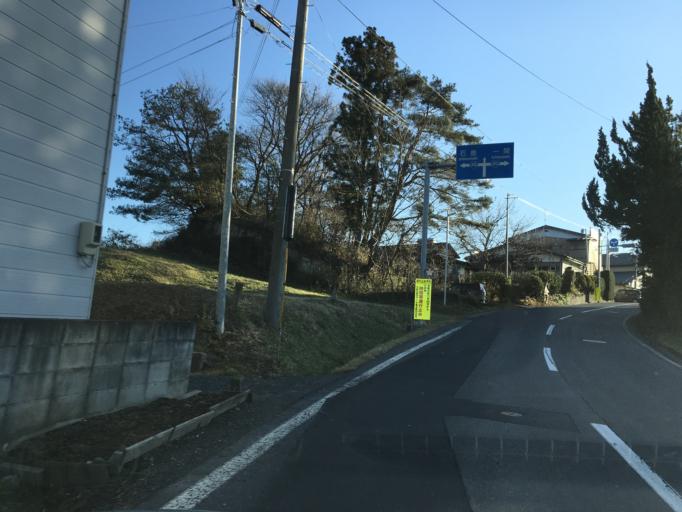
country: JP
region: Iwate
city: Ichinoseki
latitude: 38.7822
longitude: 141.2235
